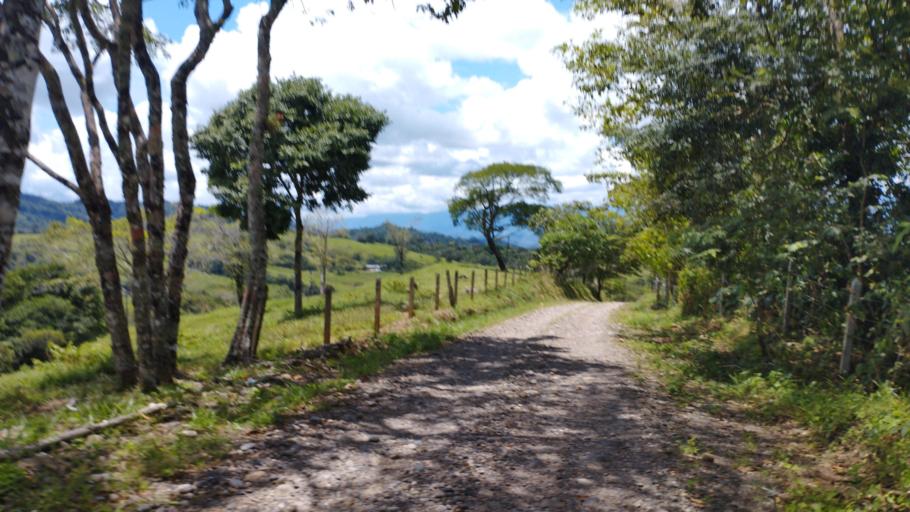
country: CO
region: Boyaca
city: San Luis de Gaceno
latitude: 4.7757
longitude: -73.1286
